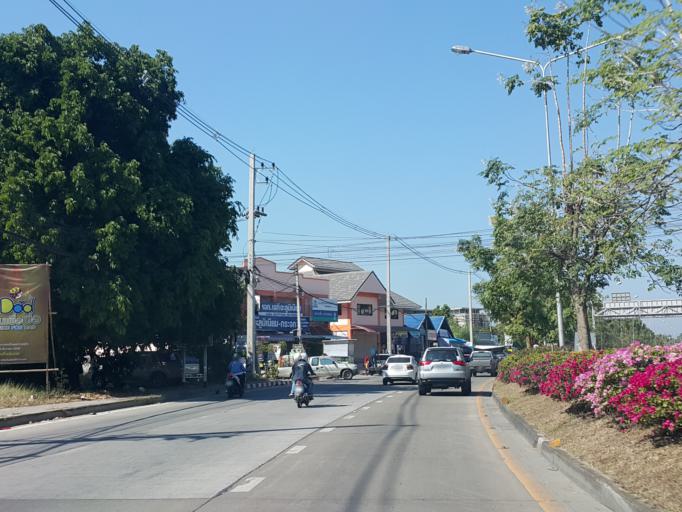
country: TH
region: Chiang Mai
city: Chiang Mai
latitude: 18.8245
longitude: 99.0079
